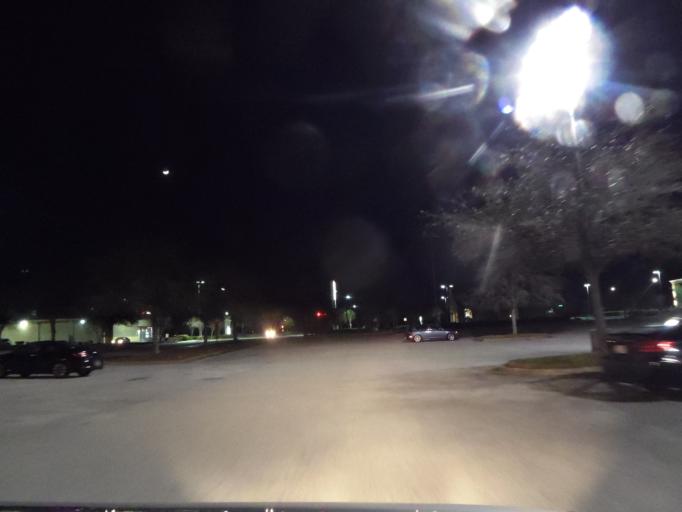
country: US
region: Florida
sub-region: Clay County
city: Orange Park
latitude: 30.2355
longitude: -81.6957
